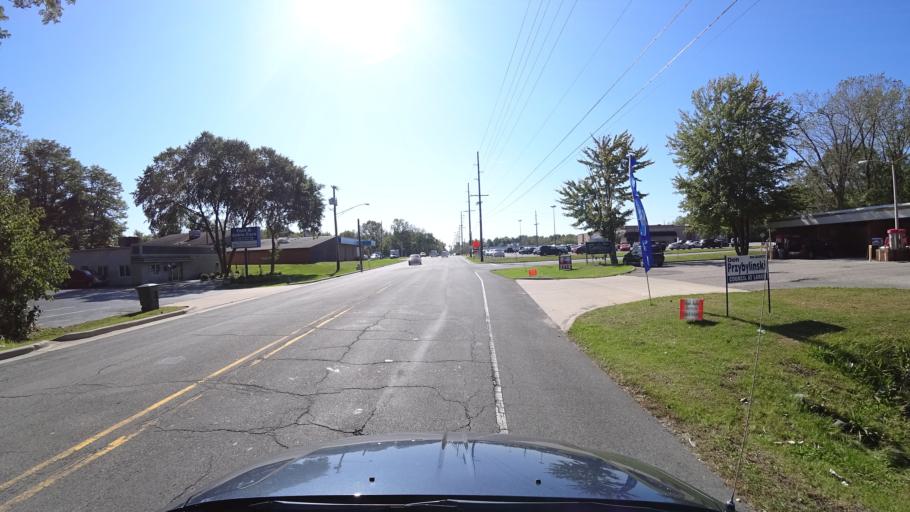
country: US
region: Indiana
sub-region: LaPorte County
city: Trail Creek
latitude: 41.6889
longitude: -86.8745
